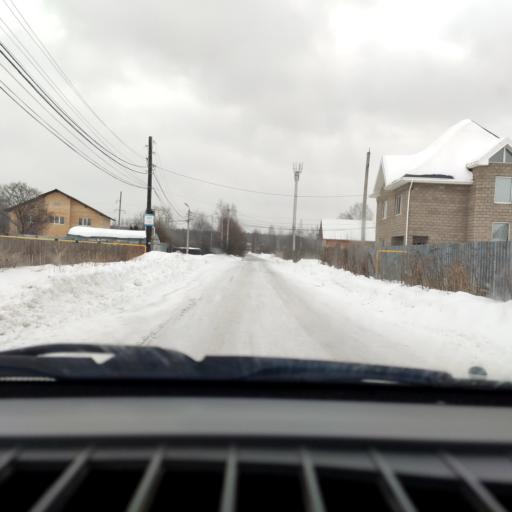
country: RU
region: Perm
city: Krasnokamsk
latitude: 58.0954
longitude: 55.8027
